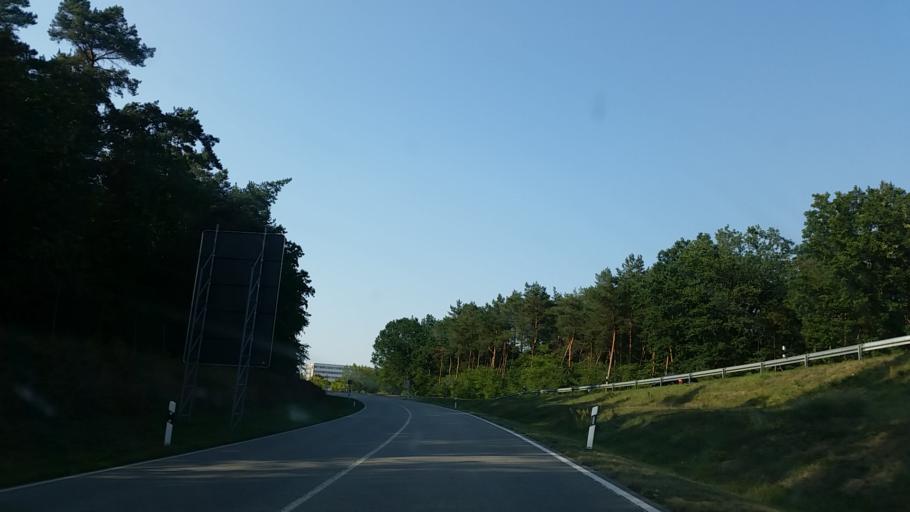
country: DE
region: Brandenburg
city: Meyenburg
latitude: 53.0848
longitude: 14.2287
